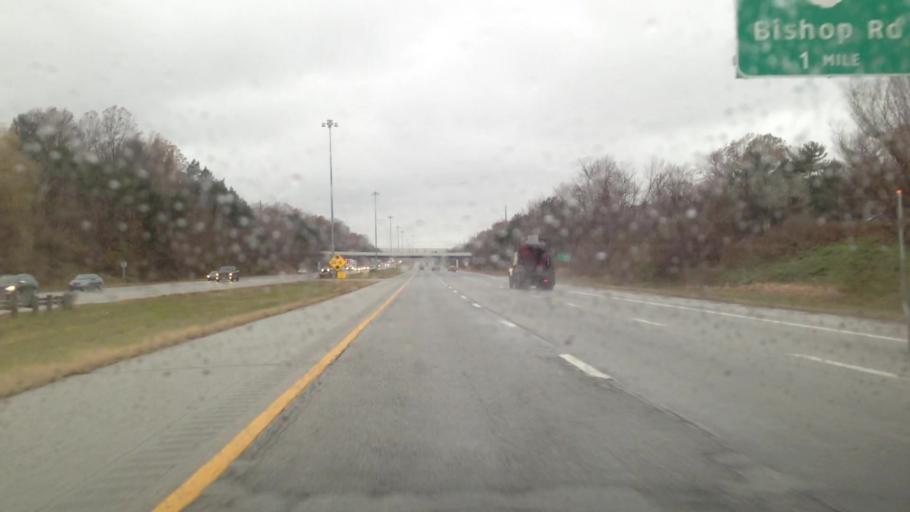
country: US
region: Ohio
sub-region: Lake County
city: Wickliffe
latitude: 41.5907
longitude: -81.4574
